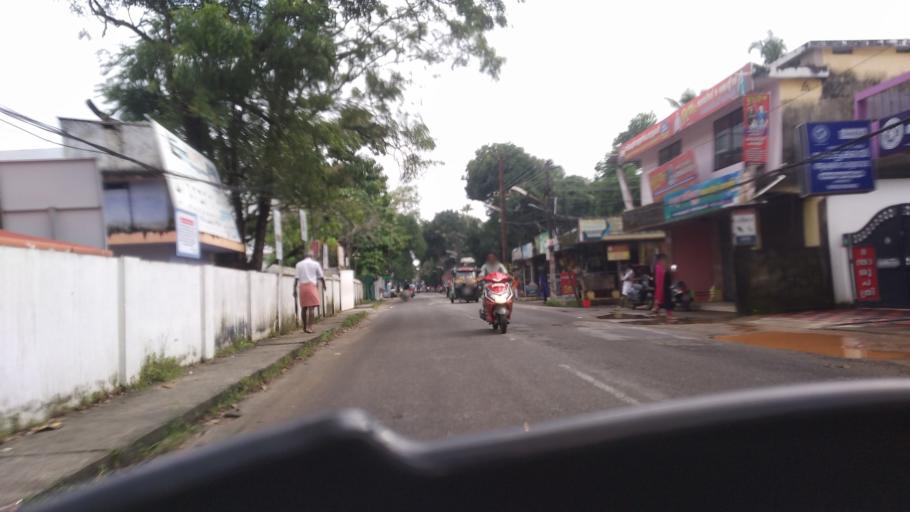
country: IN
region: Kerala
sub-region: Ernakulam
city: Elur
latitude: 10.0855
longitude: 76.2091
